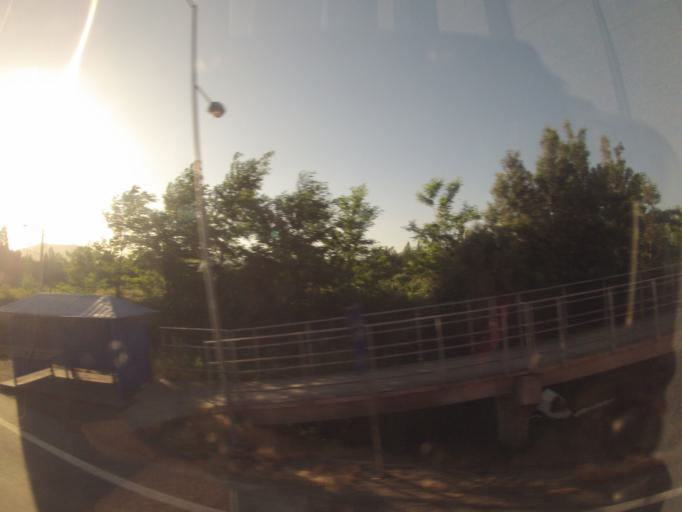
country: CL
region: O'Higgins
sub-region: Provincia de Colchagua
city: Chimbarongo
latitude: -34.6650
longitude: -70.9958
